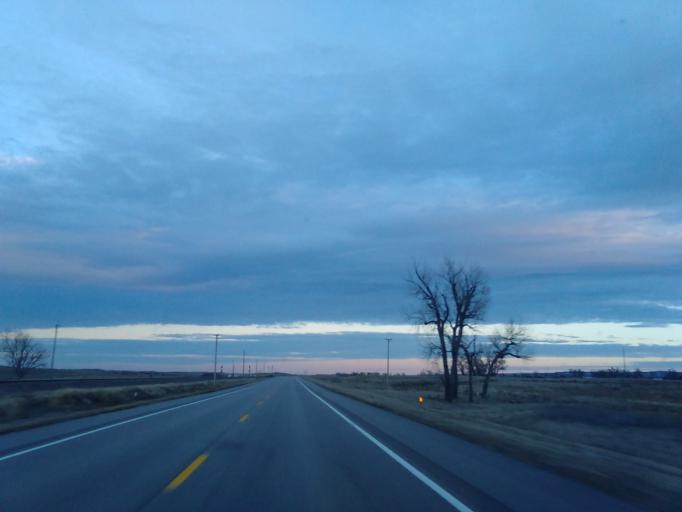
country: US
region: Nebraska
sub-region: Garden County
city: Oshkosh
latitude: 41.3878
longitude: -102.2908
